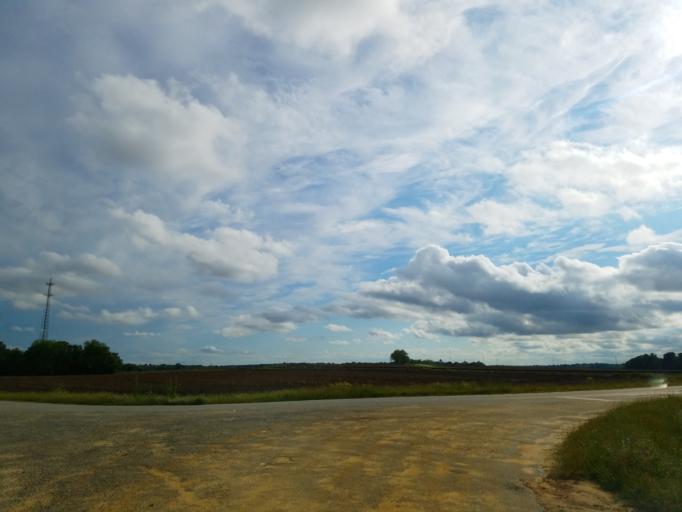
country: US
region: Georgia
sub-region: Dooly County
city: Vienna
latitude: 32.1726
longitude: -83.7654
